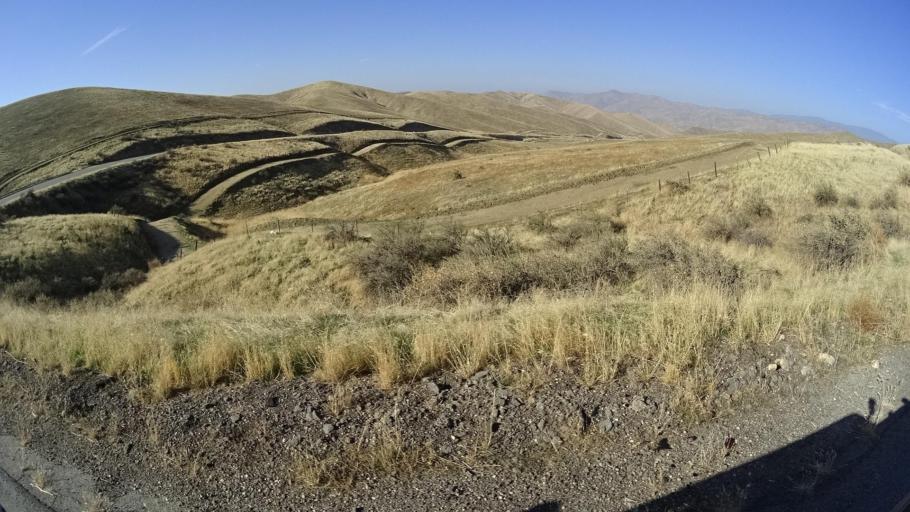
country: US
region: California
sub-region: Kern County
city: Bear Valley Springs
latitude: 35.2766
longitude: -118.6933
